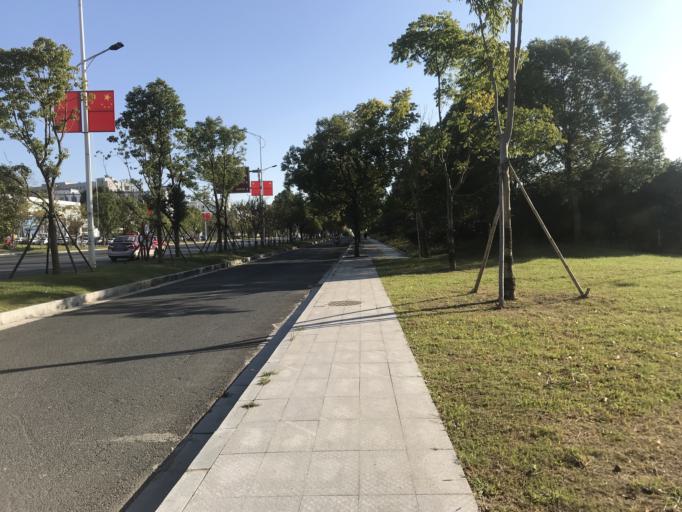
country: CN
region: Anhui Sheng
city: Xintan
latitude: 29.7716
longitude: 118.2587
